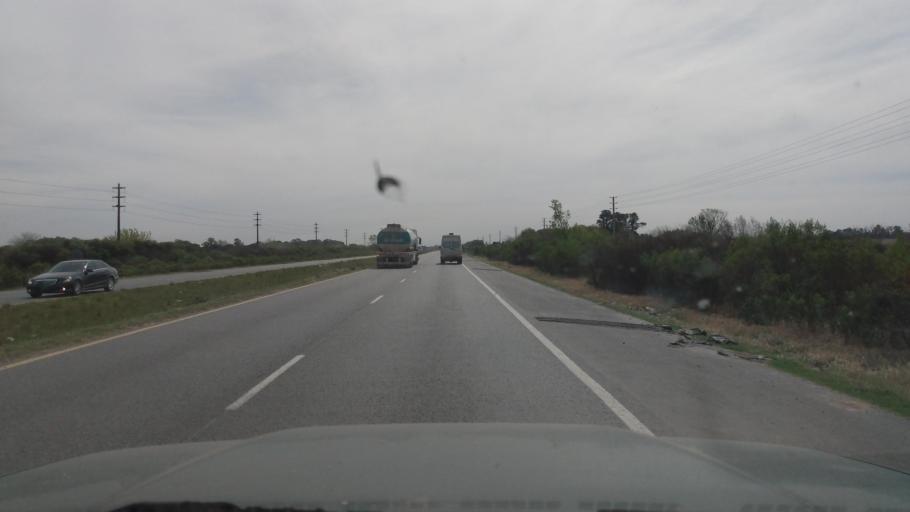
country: AR
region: Buenos Aires
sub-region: Partido de Lujan
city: Lujan
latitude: -34.5466
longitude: -59.0368
